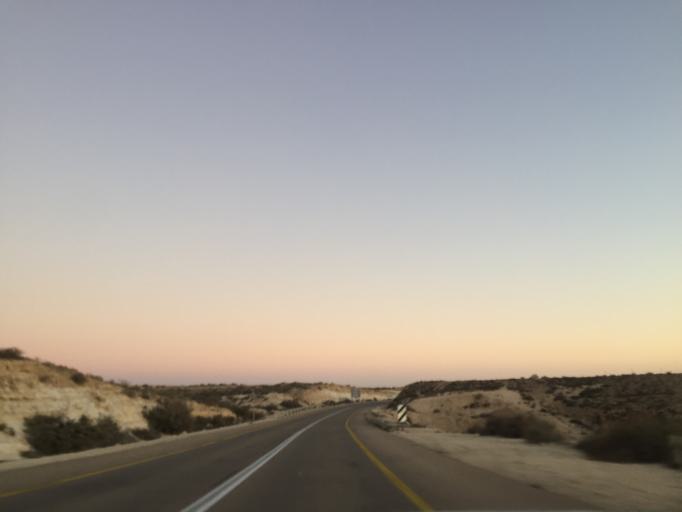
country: IL
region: Southern District
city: Midreshet Ben-Gurion
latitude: 30.8934
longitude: 34.7895
